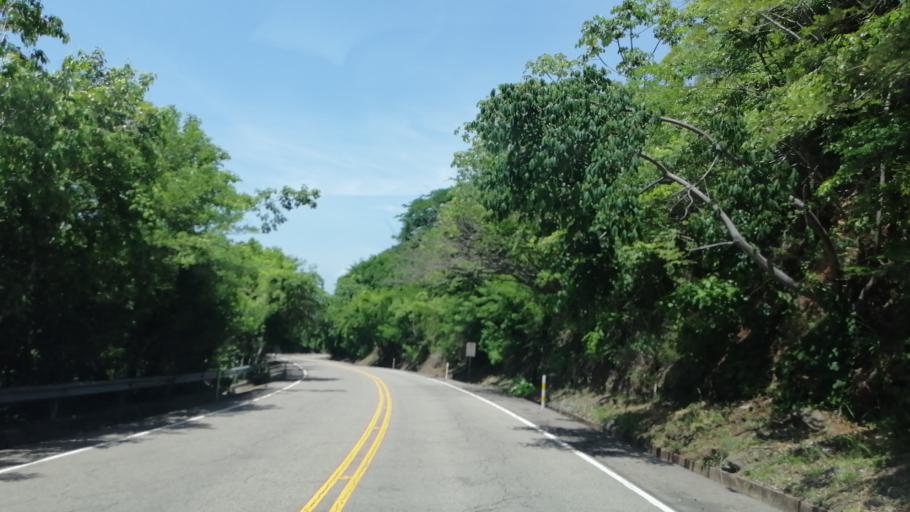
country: SV
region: Chalatenango
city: Nueva Concepcion
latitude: 14.1620
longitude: -89.3135
